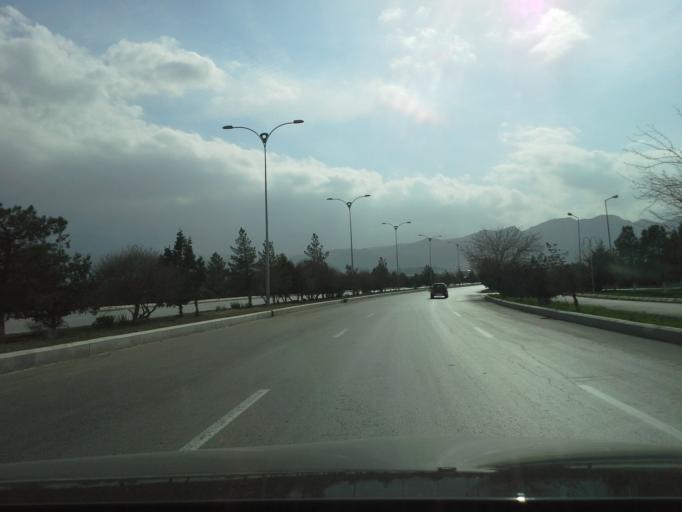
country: TM
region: Ahal
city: Abadan
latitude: 37.9749
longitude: 58.2433
